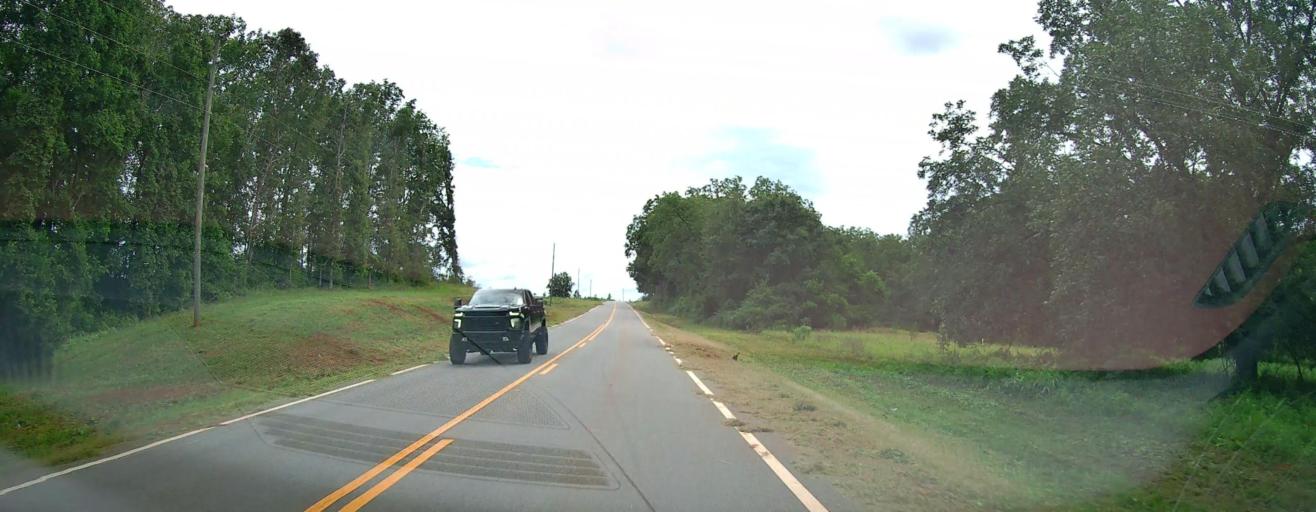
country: US
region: Georgia
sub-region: Macon County
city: Oglethorpe
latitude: 32.2715
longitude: -84.1837
